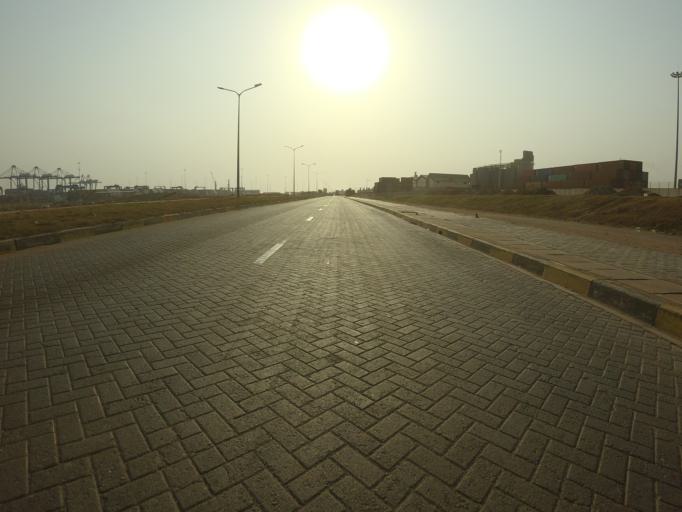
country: GH
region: Greater Accra
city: Tema
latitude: 5.6229
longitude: -0.0103
